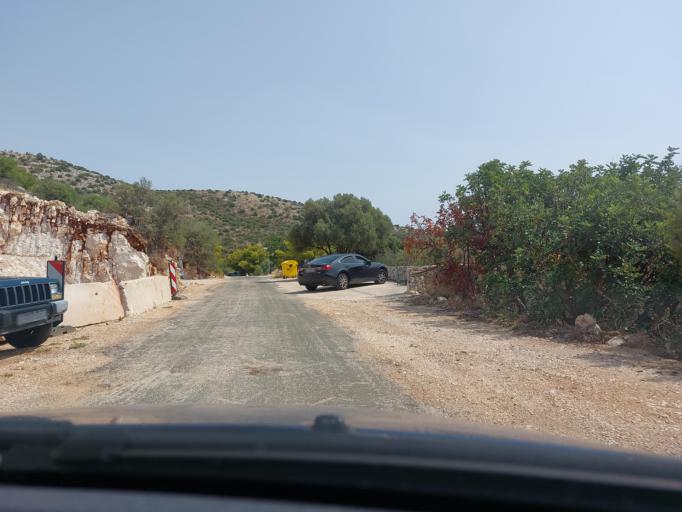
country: HR
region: Dubrovacko-Neretvanska
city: Smokvica
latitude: 42.7351
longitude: 16.8898
